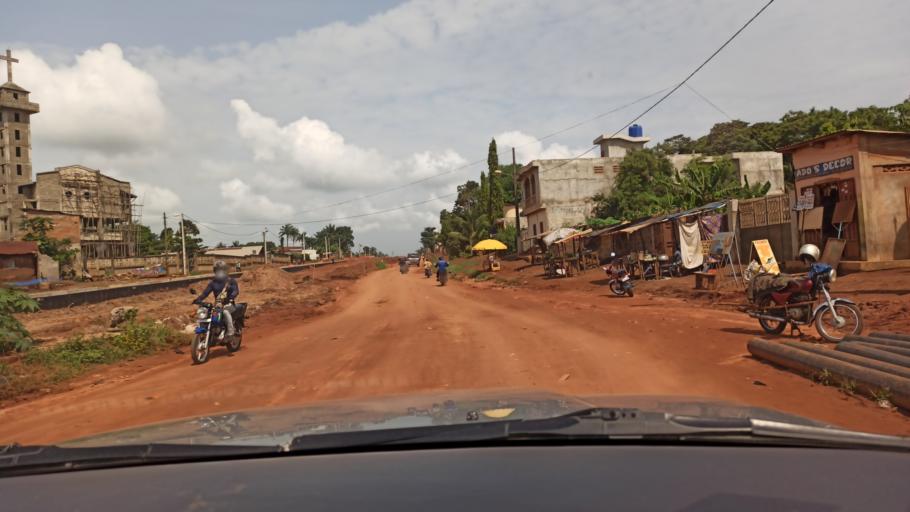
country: BJ
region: Queme
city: Porto-Novo
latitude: 6.4778
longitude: 2.5939
